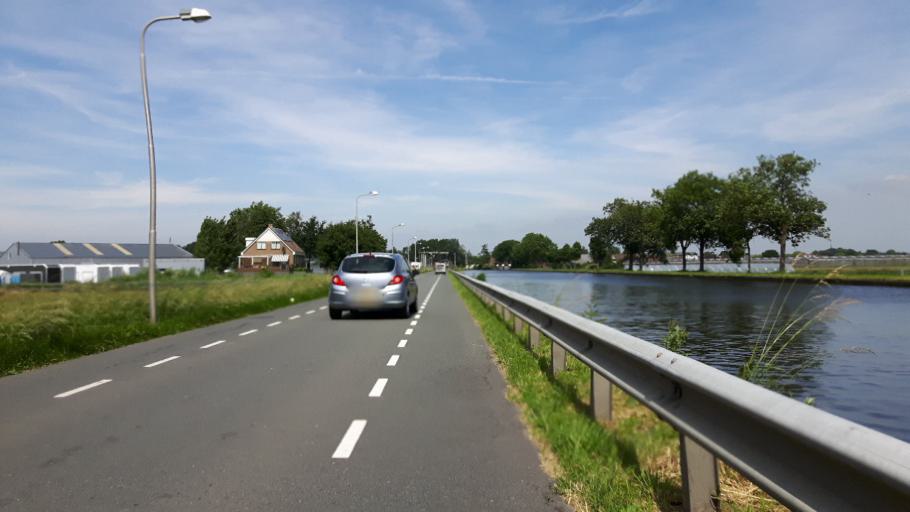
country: NL
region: South Holland
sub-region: Gemeente Nieuwkoop
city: Nieuwkoop
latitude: 52.1911
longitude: 4.7360
